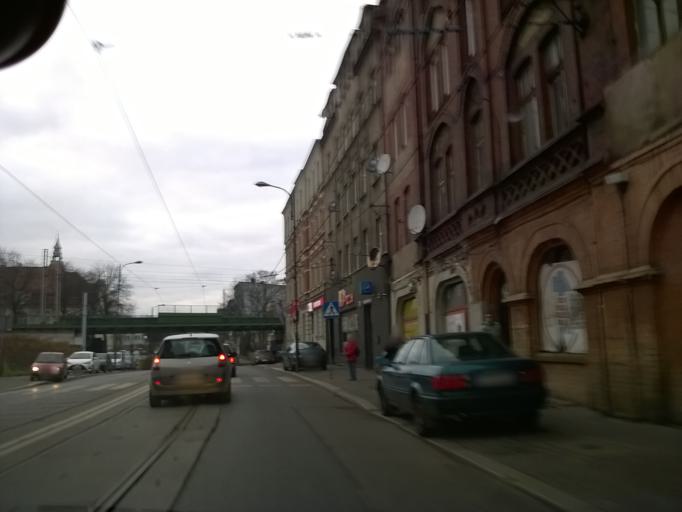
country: PL
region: Silesian Voivodeship
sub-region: Swietochlowice
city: Swietochlowice
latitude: 50.2848
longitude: 18.9336
